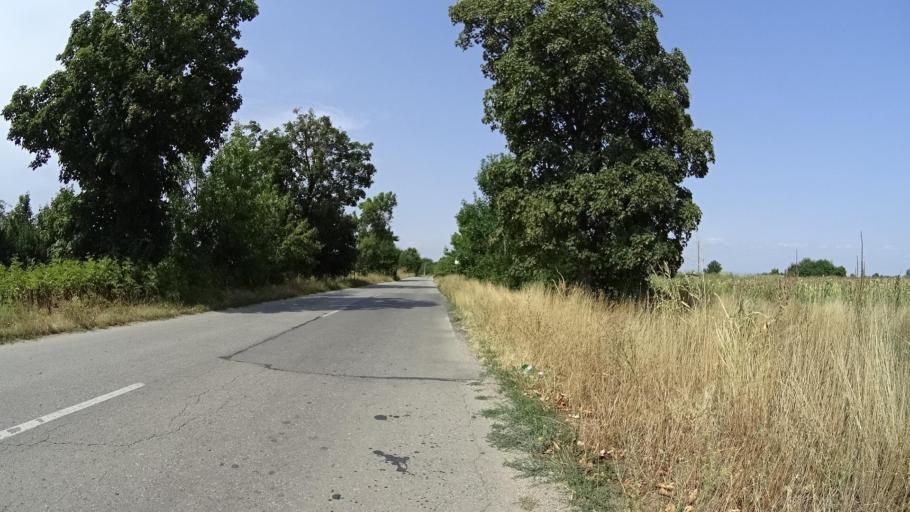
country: BG
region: Plovdiv
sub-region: Obshtina Kaloyanovo
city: Kaloyanovo
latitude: 42.2618
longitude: 24.8007
